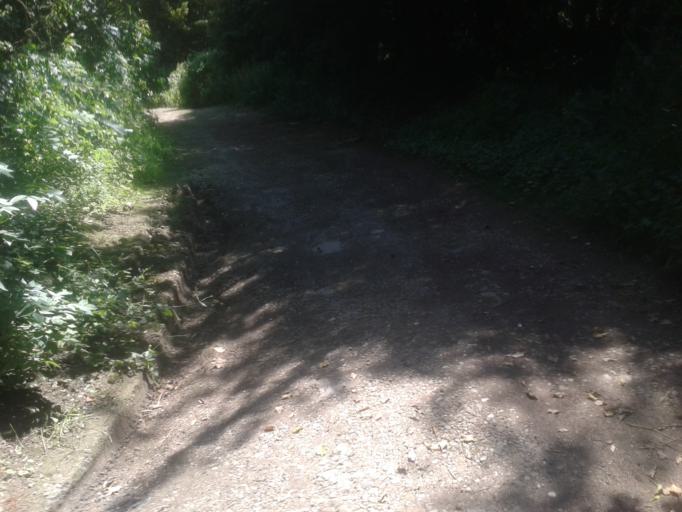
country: GB
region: England
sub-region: East Riding of Yorkshire
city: Londesborough
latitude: 53.8982
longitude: -0.6768
